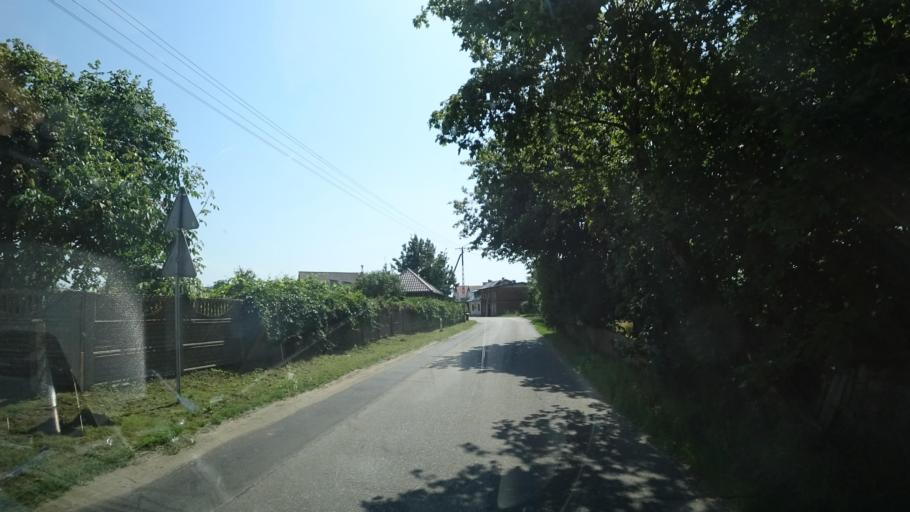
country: PL
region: Pomeranian Voivodeship
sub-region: Powiat chojnicki
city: Brusy
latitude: 53.8705
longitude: 17.6703
